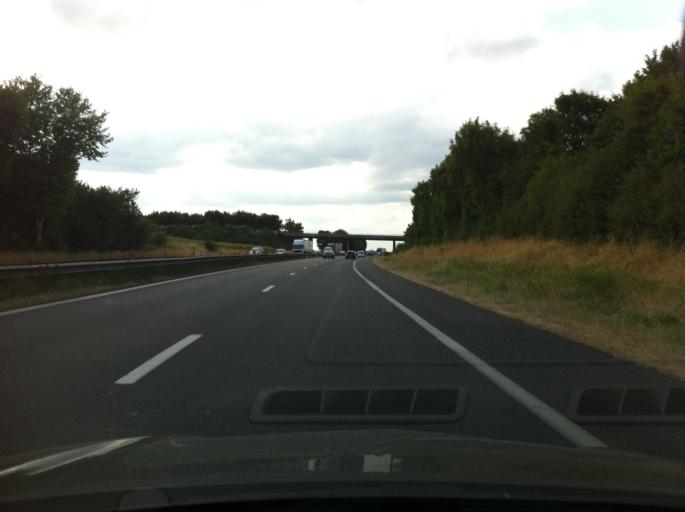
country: FR
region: Ile-de-France
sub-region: Departement de Seine-et-Marne
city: Brie-Comte-Robert
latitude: 48.6835
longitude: 2.6007
